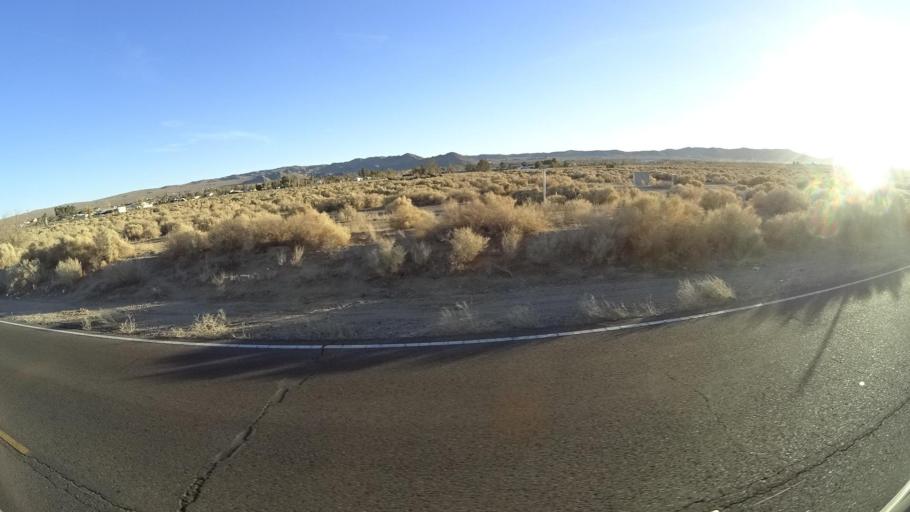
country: US
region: California
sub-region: Kern County
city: Ridgecrest
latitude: 35.6081
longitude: -117.6601
